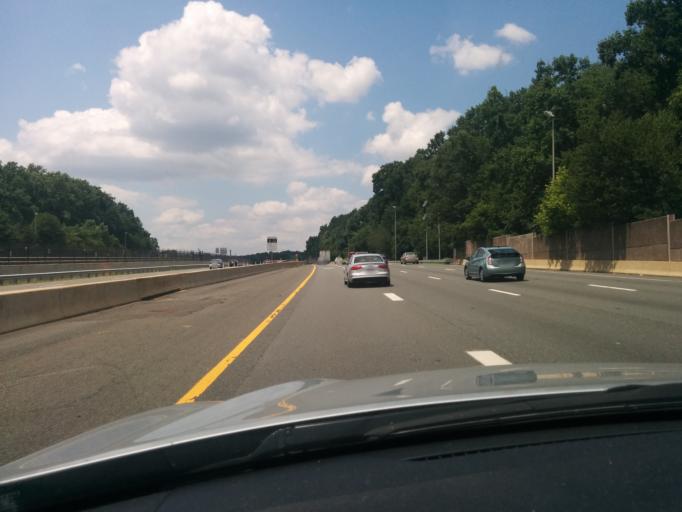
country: US
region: Virginia
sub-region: Fairfax County
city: Wolf Trap
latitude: 38.9476
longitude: -77.2988
